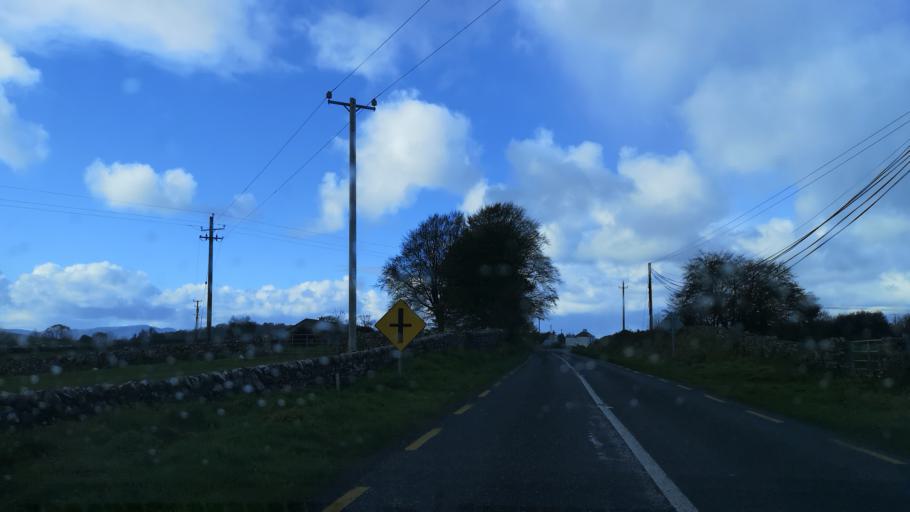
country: IE
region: Connaught
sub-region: Maigh Eo
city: Westport
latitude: 53.7787
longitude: -9.4234
